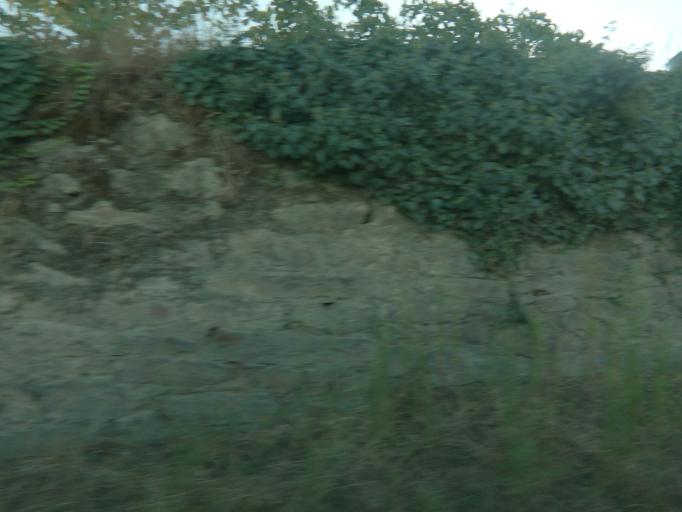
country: PT
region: Vila Real
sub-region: Santa Marta de Penaguiao
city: Santa Marta de Penaguiao
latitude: 41.1984
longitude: -7.7688
